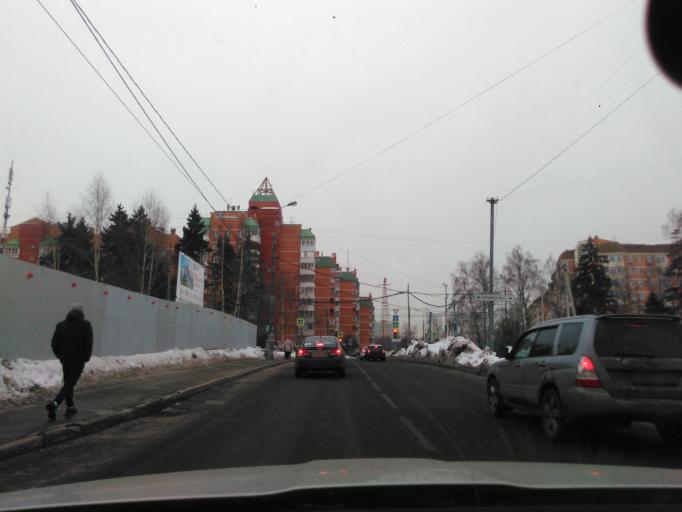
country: RU
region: Moscow
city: Khimki
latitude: 55.8865
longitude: 37.3928
